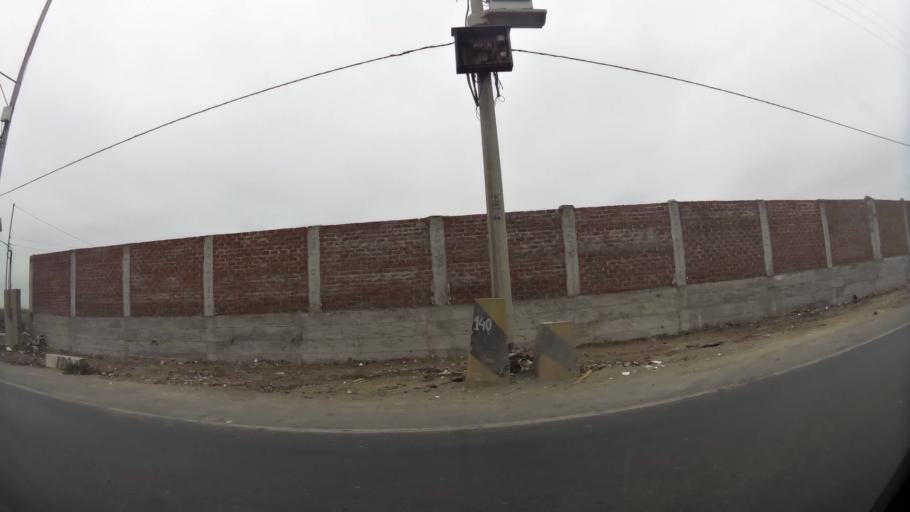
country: PE
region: La Libertad
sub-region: Provincia de Trujillo
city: Buenos Aires
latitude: -8.1367
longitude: -79.0586
